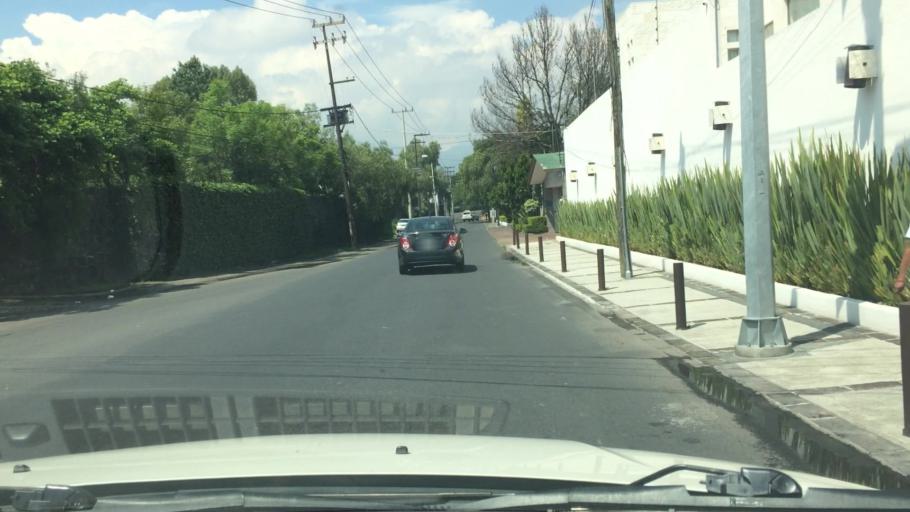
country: MX
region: Mexico City
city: Magdalena Contreras
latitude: 19.3282
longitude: -99.2076
